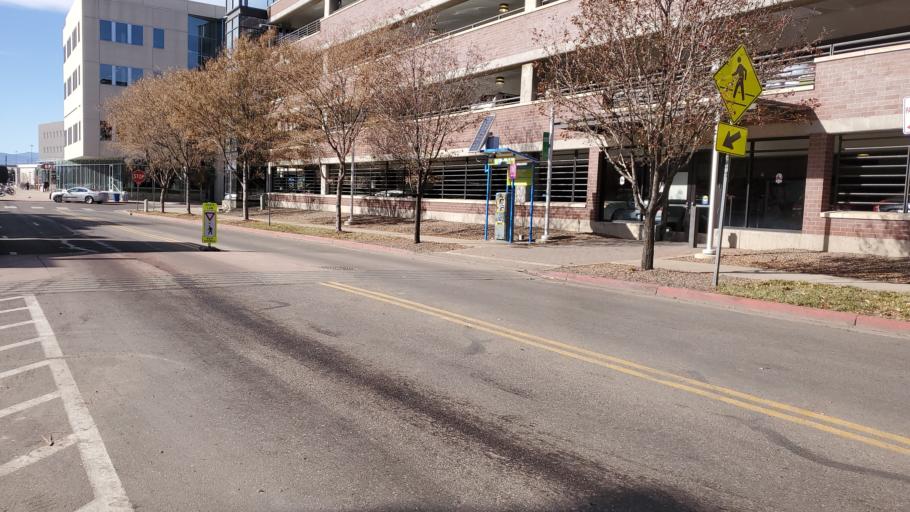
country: US
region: Colorado
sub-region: Denver County
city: Denver
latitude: 39.7458
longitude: -105.0061
